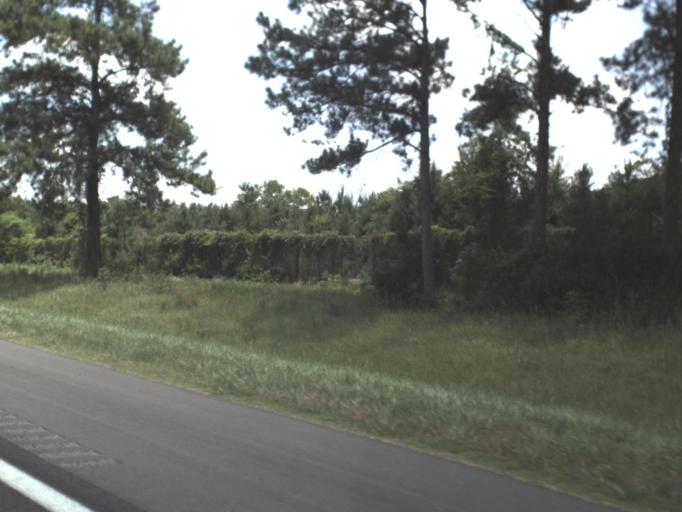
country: US
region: Florida
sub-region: Madison County
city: Madison
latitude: 30.4133
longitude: -83.4310
